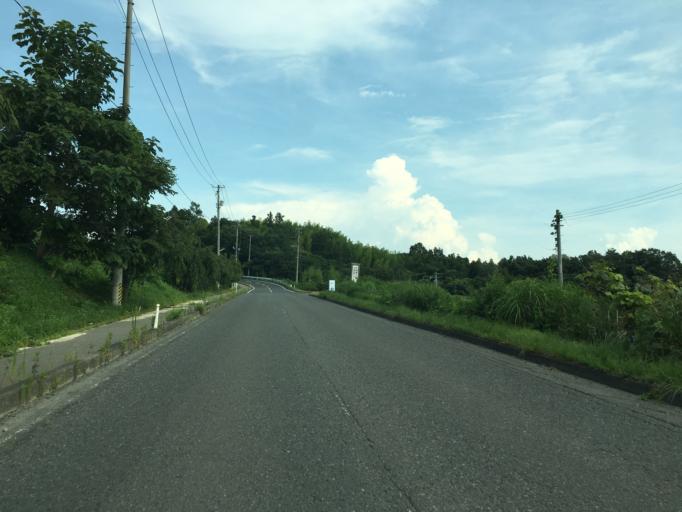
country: JP
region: Fukushima
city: Motomiya
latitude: 37.4895
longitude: 140.4137
